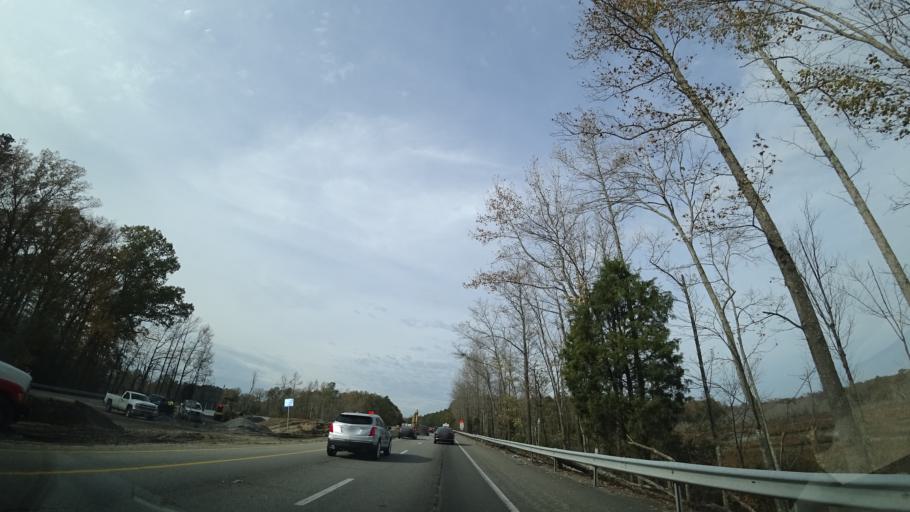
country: US
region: Virginia
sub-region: Henrico County
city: Sandston
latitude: 37.5175
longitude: -77.1981
